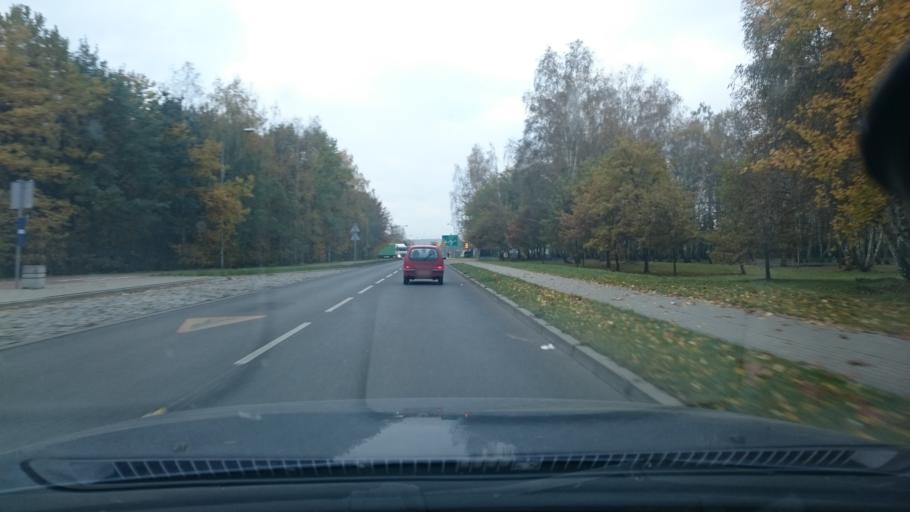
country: PL
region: Silesian Voivodeship
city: Zebrzydowice
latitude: 50.1037
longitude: 18.5165
